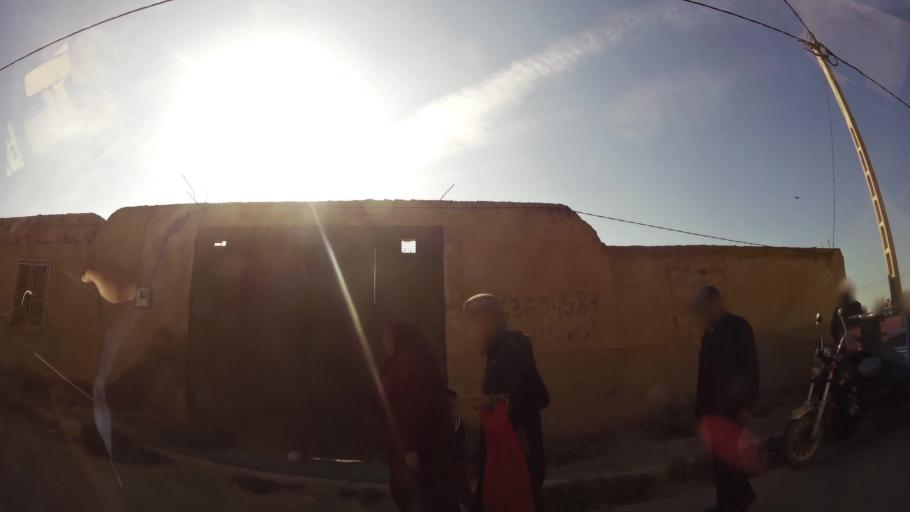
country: MA
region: Oriental
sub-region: Oujda-Angad
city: Oujda
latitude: 34.7210
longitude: -1.8926
